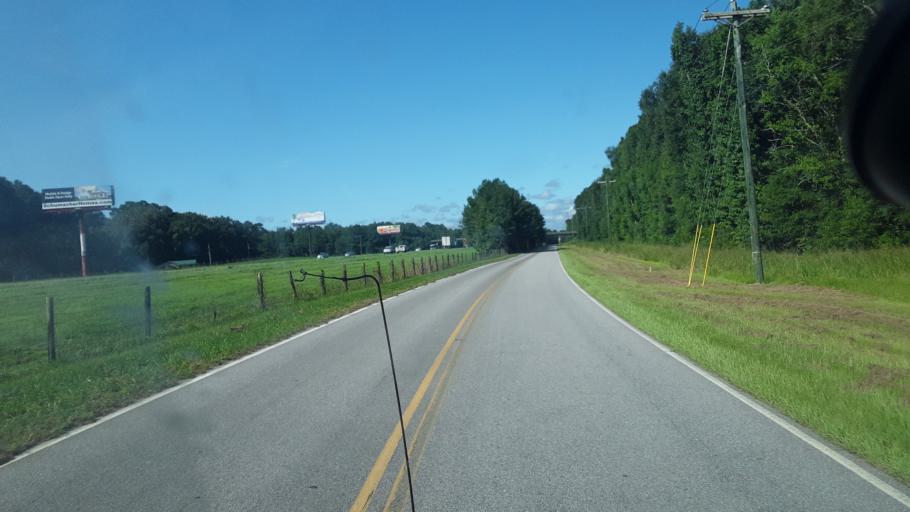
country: US
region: South Carolina
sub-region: Hampton County
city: Yemassee
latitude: 32.5974
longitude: -80.9088
